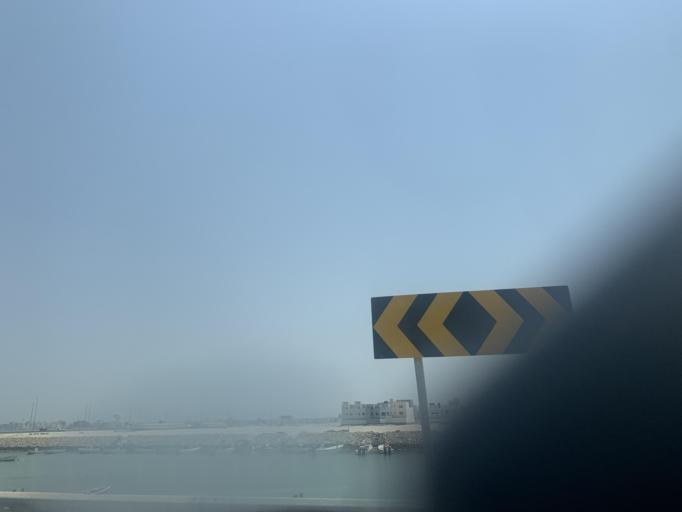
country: BH
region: Muharraq
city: Al Muharraq
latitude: 26.2959
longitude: 50.6396
